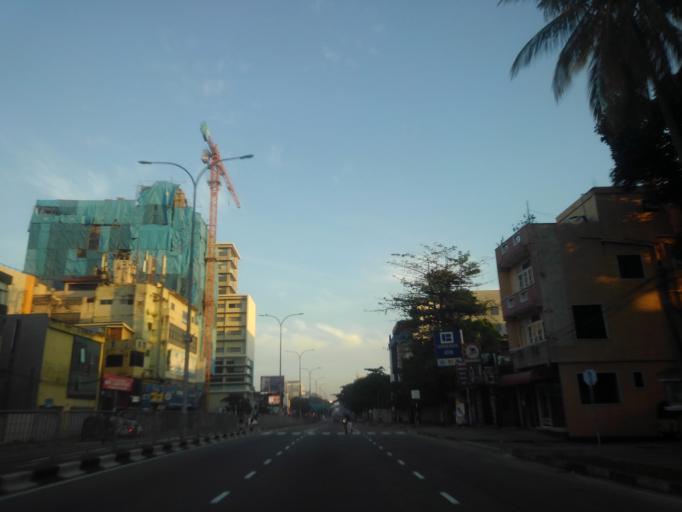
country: LK
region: Western
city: Pita Kotte
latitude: 6.9047
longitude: 79.8773
